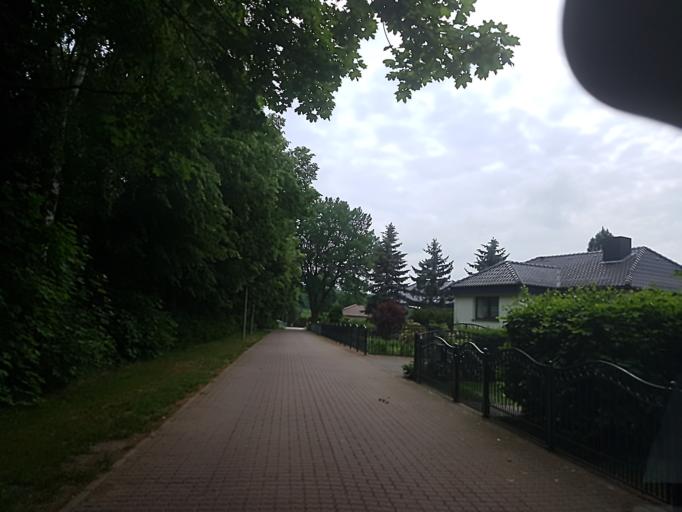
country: DE
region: Saxony-Anhalt
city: Lindau
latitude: 52.0806
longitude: 12.2453
